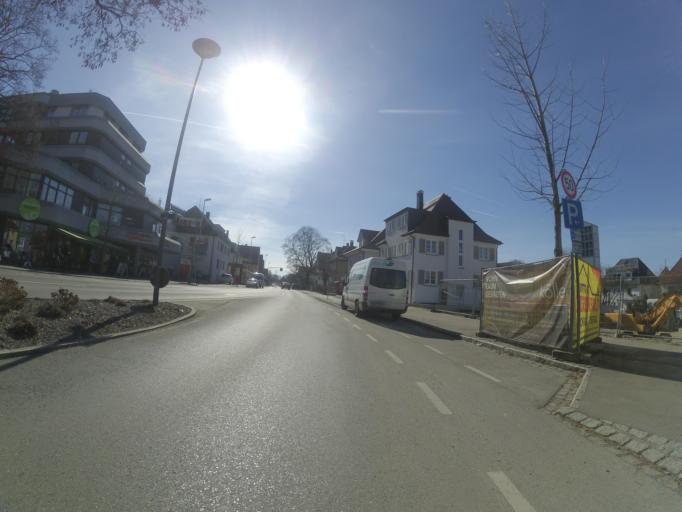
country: DE
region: Baden-Wuerttemberg
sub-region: Tuebingen Region
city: Ravensburg
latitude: 47.7740
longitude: 9.6087
